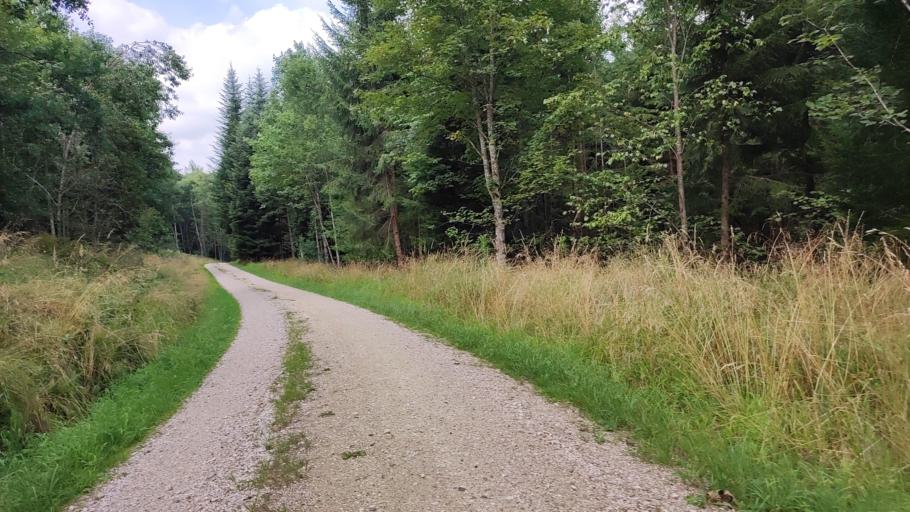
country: DE
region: Bavaria
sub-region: Swabia
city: Landensberg
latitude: 48.4219
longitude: 10.5144
